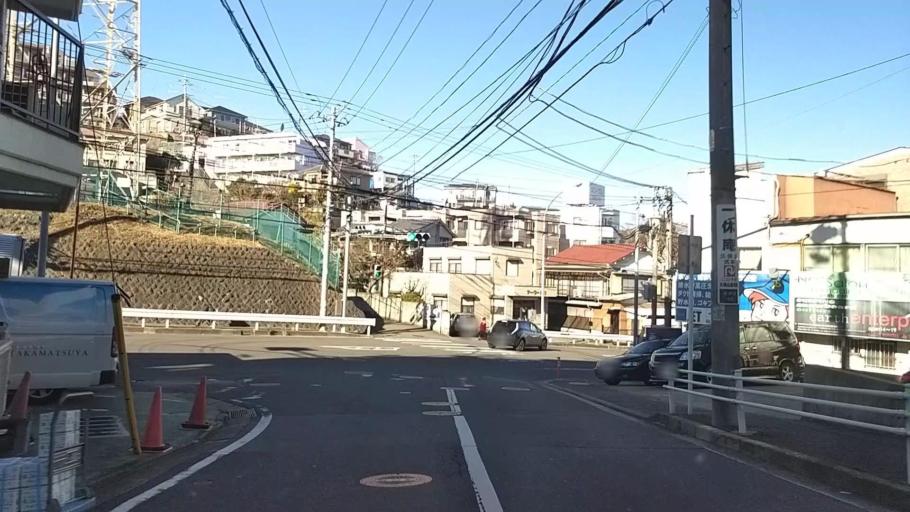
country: JP
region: Kanagawa
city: Yokohama
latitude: 35.4417
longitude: 139.5964
